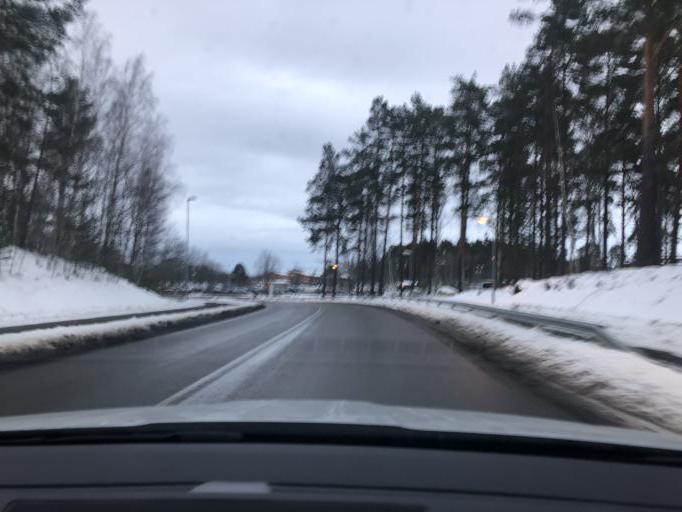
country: SE
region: OEstergoetland
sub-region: Norrkopings Kommun
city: Norrkoping
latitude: 58.5632
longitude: 16.1745
